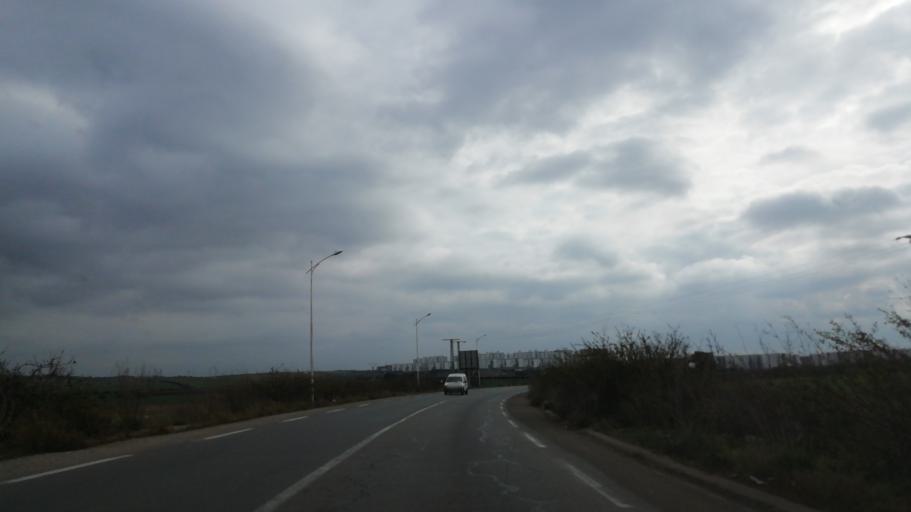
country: DZ
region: Oran
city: Sidi ech Chahmi
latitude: 35.5661
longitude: -0.4479
